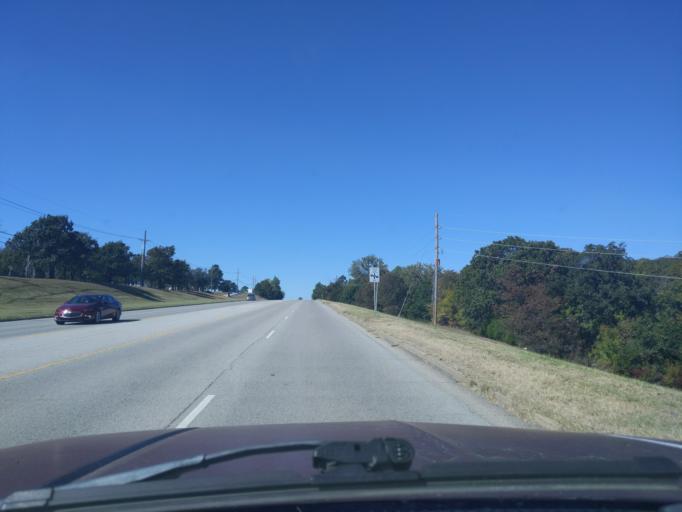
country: US
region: Oklahoma
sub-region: Tulsa County
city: Glenpool
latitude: 35.9884
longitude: -96.0405
